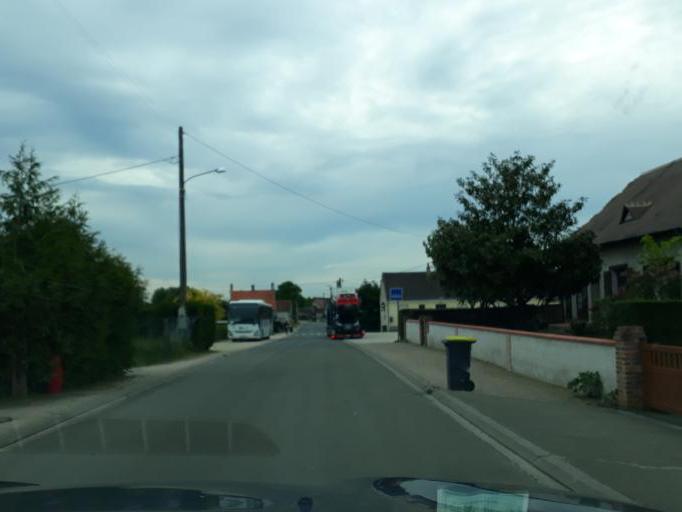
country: FR
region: Centre
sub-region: Departement du Loir-et-Cher
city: Dhuizon
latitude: 47.5865
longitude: 1.6558
